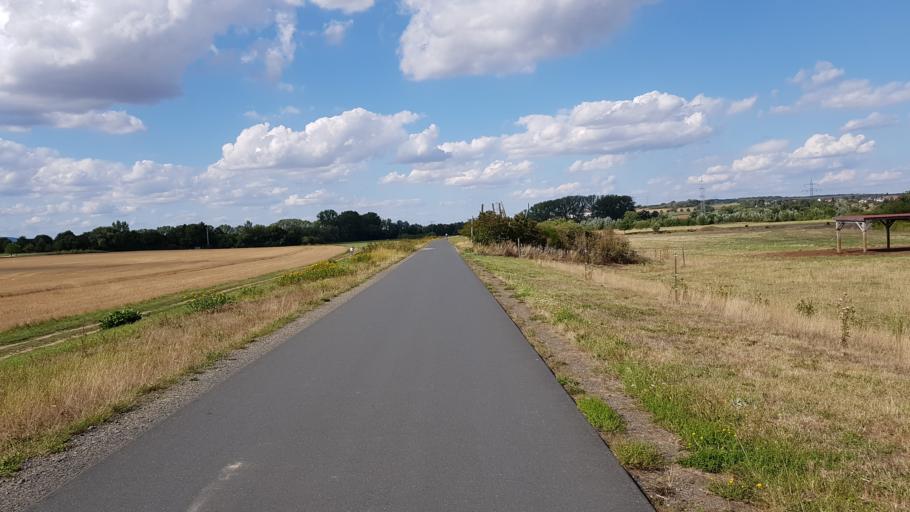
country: DE
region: Hesse
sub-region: Regierungsbezirk Darmstadt
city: Niederdorfelden
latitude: 50.2015
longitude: 8.7725
